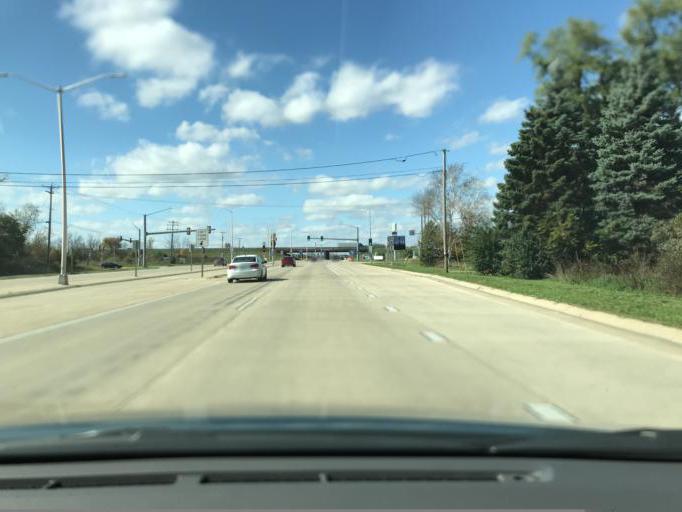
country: US
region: Wisconsin
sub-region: Kenosha County
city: Somers
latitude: 42.6133
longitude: -87.9474
